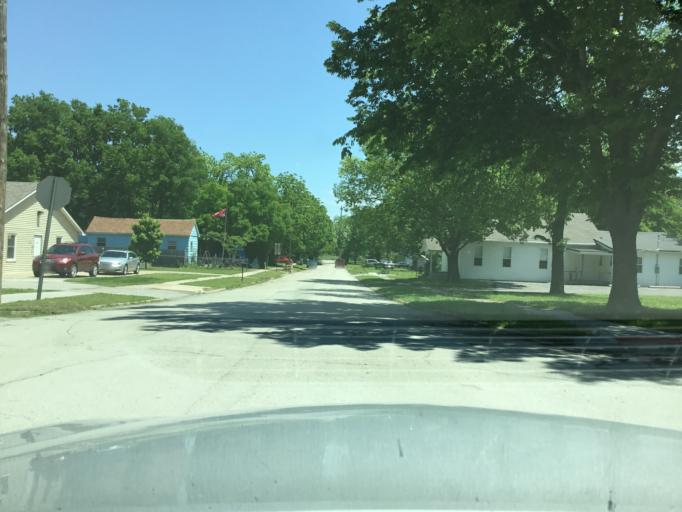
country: US
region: Kansas
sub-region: Montgomery County
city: Independence
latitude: 37.2188
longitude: -95.6956
